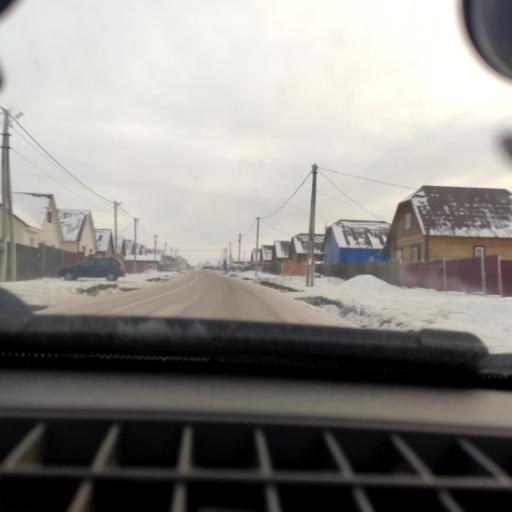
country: RU
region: Bashkortostan
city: Iglino
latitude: 54.8284
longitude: 56.4363
